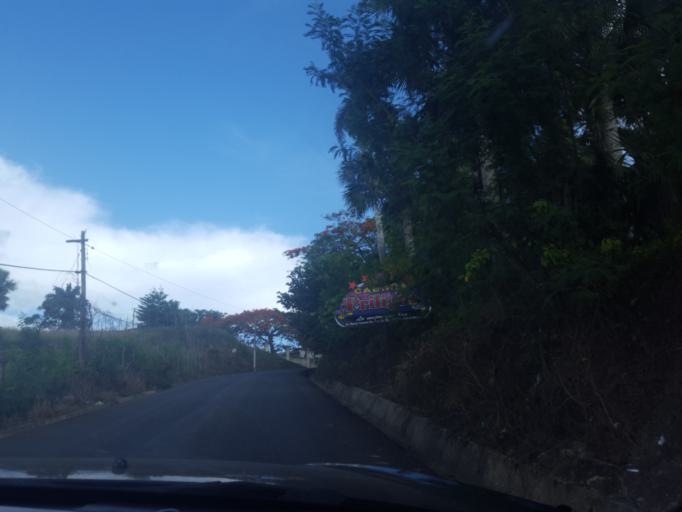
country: DO
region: La Vega
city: Rio Verde Arriba
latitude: 19.3547
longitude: -70.6302
